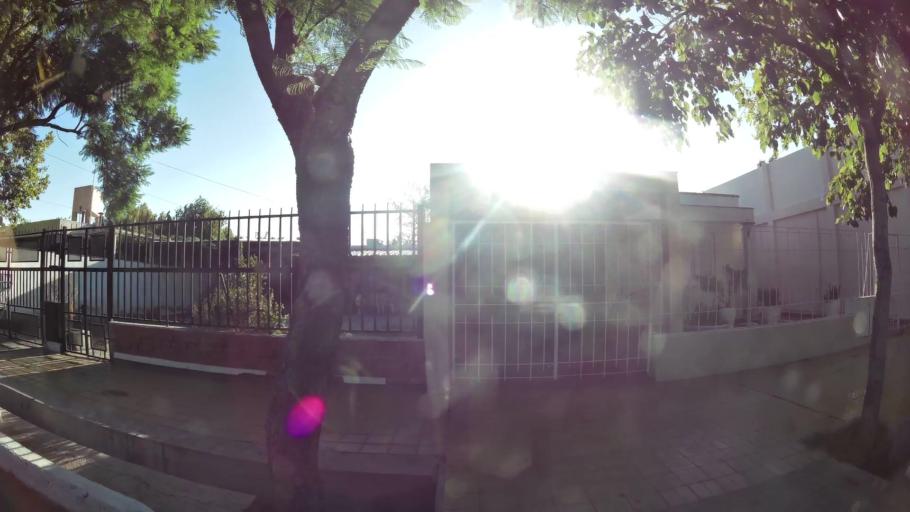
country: AR
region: San Juan
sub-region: Departamento de Santa Lucia
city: Santa Lucia
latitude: -31.5385
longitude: -68.5065
